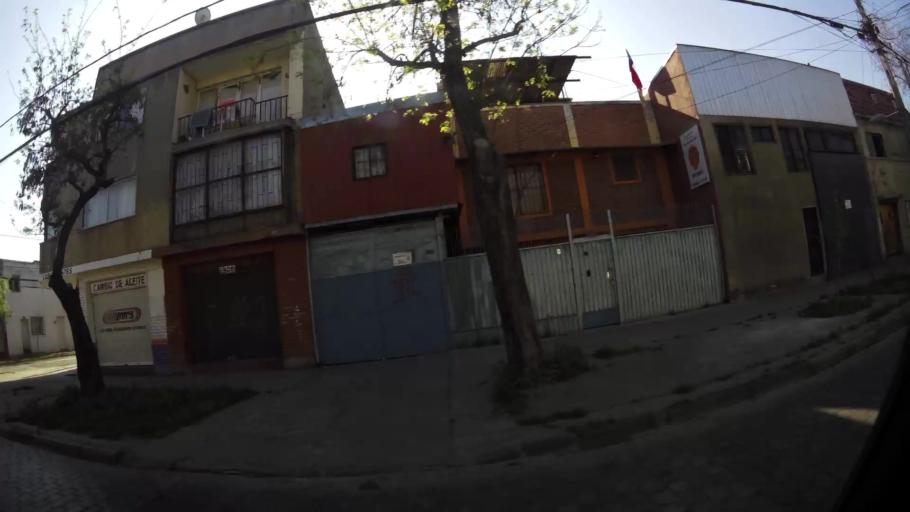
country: CL
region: Santiago Metropolitan
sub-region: Provincia de Santiago
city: Santiago
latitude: -33.4693
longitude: -70.6298
